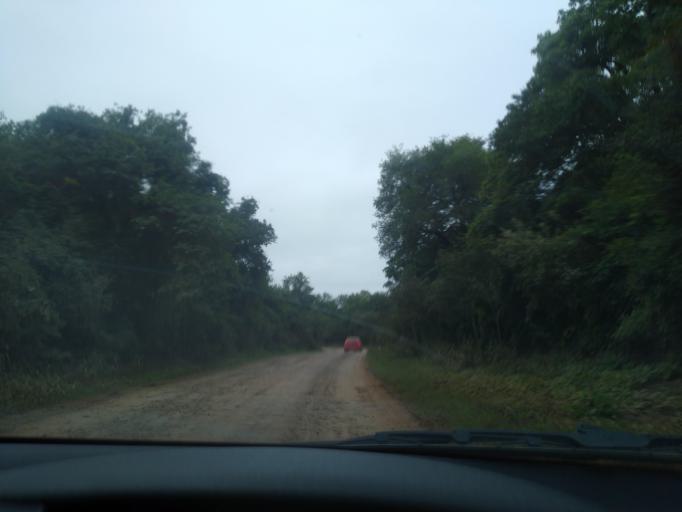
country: AR
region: Chaco
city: Colonia Benitez
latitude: -27.3386
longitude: -58.9686
